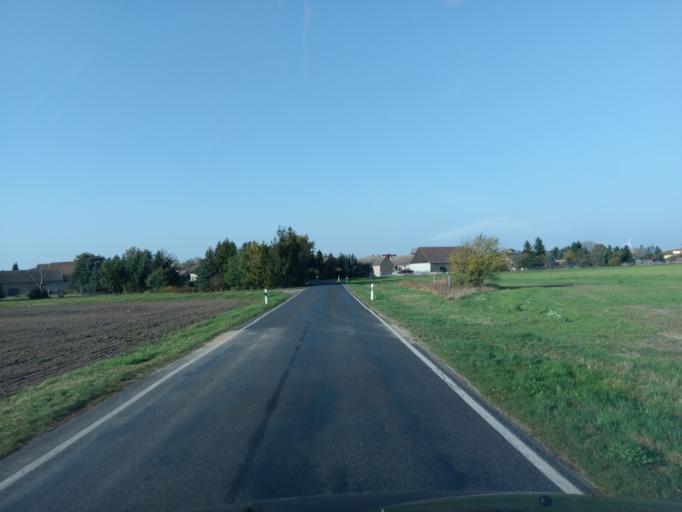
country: DE
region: Brandenburg
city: Falkenberg
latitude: 51.5269
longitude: 13.2991
